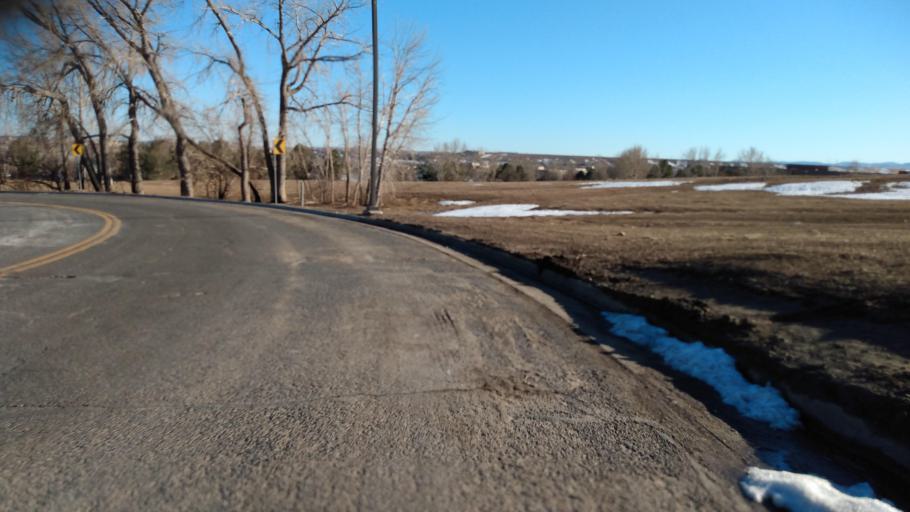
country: US
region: Colorado
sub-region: Boulder County
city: Superior
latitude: 39.9699
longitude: -105.1711
